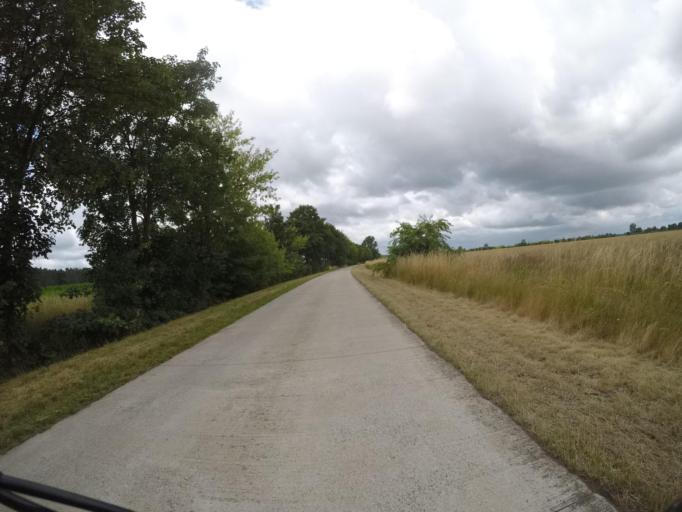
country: DE
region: Lower Saxony
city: Damnatz
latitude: 53.1951
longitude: 11.1173
